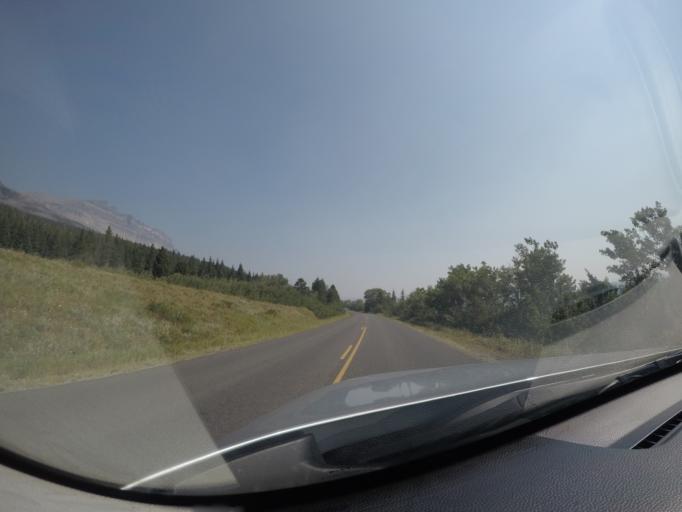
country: US
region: Montana
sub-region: Glacier County
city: Browning
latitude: 48.6970
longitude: -113.5102
